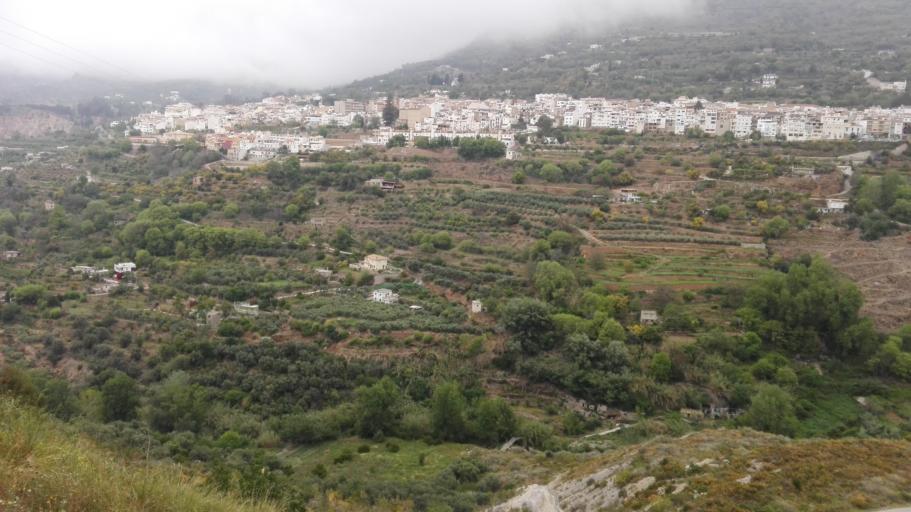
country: ES
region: Andalusia
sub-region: Provincia de Granada
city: Lanjaron
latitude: 36.9128
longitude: -3.4763
